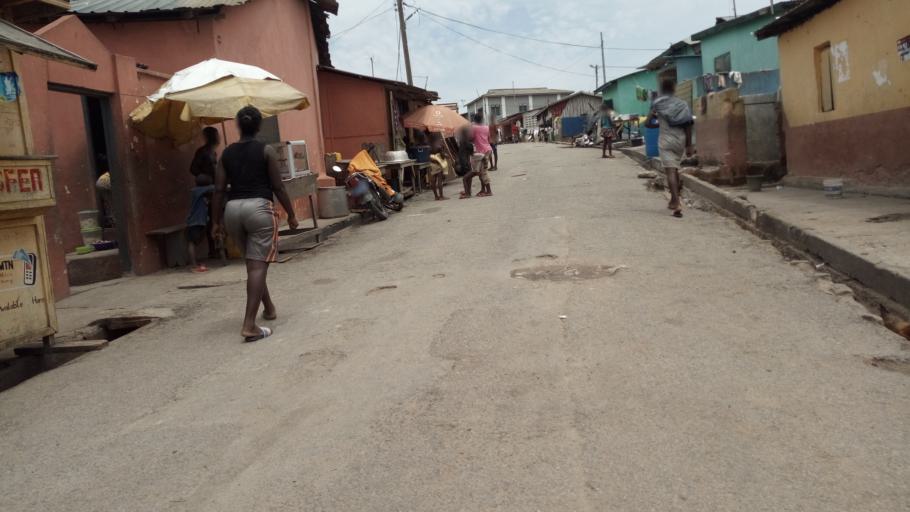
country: GH
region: Central
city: Winneba
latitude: 5.3400
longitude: -0.6208
